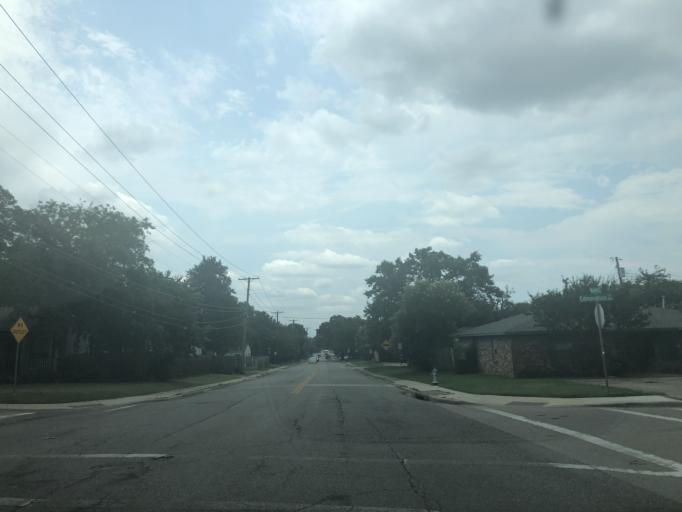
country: US
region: Texas
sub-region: Dallas County
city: Irving
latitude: 32.8049
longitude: -96.9347
